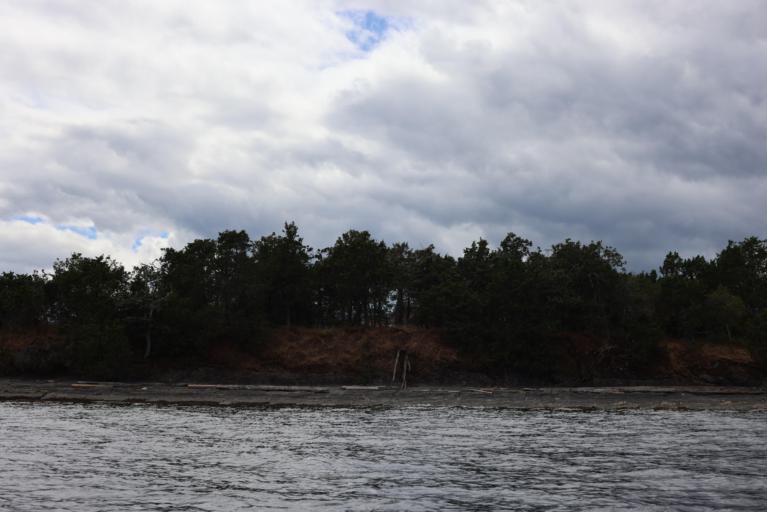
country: CA
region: British Columbia
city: North Cowichan
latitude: 48.8817
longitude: -123.6312
